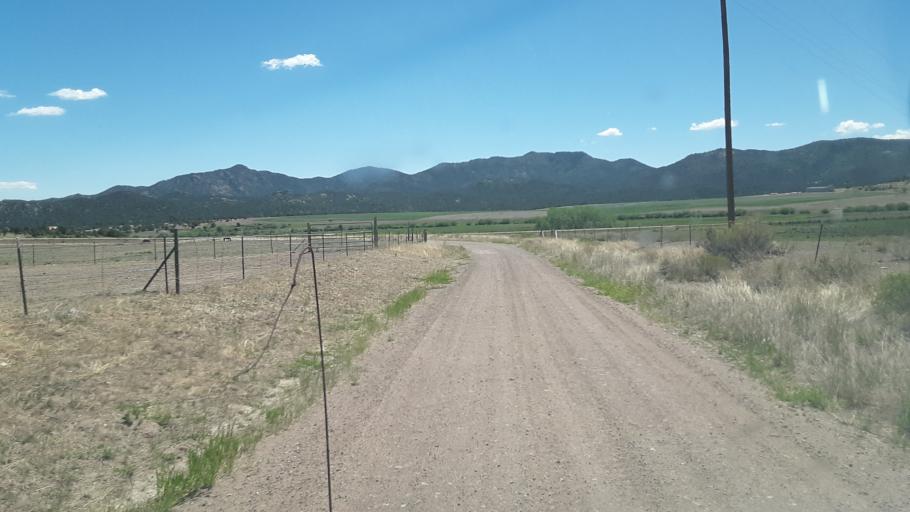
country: US
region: Colorado
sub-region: Custer County
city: Westcliffe
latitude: 38.2920
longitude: -105.6240
